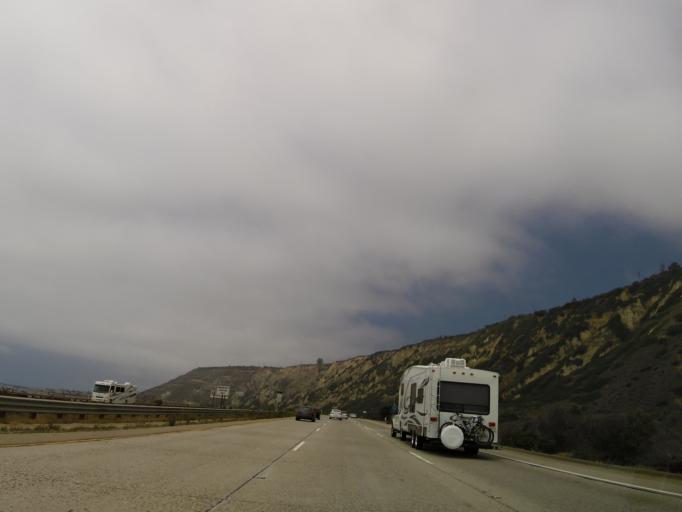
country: US
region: California
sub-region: Santa Barbara County
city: Carpinteria
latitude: 34.3476
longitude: -119.4230
